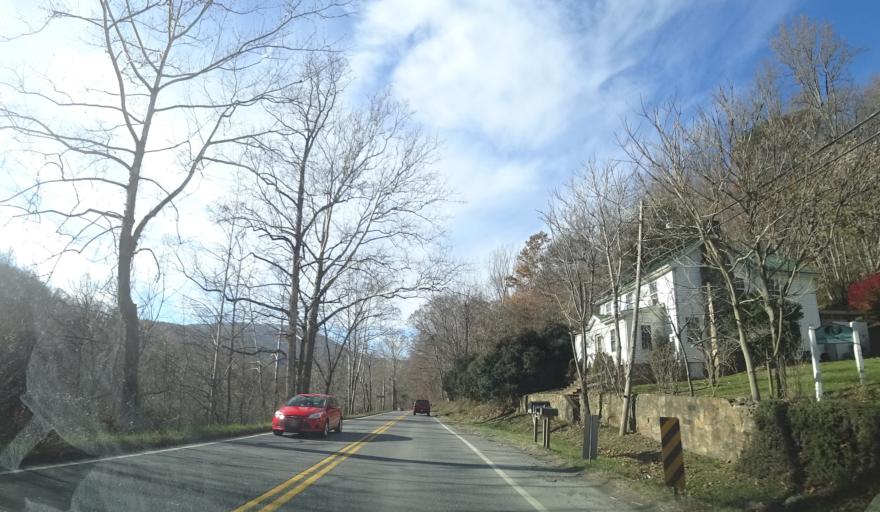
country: US
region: Virginia
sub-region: Greene County
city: Stanardsville
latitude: 38.3304
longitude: -78.4901
